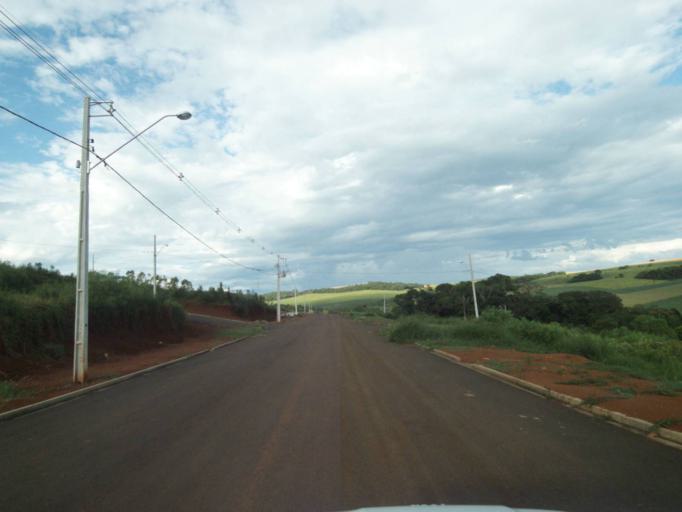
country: BR
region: Parana
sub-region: Laranjeiras Do Sul
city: Laranjeiras do Sul
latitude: -25.4905
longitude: -52.5232
